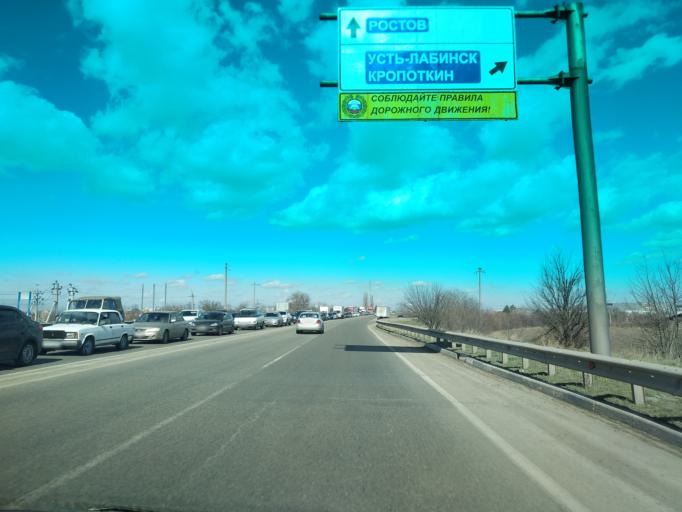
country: RU
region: Krasnodarskiy
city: Pashkovskiy
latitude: 45.0018
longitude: 39.1152
